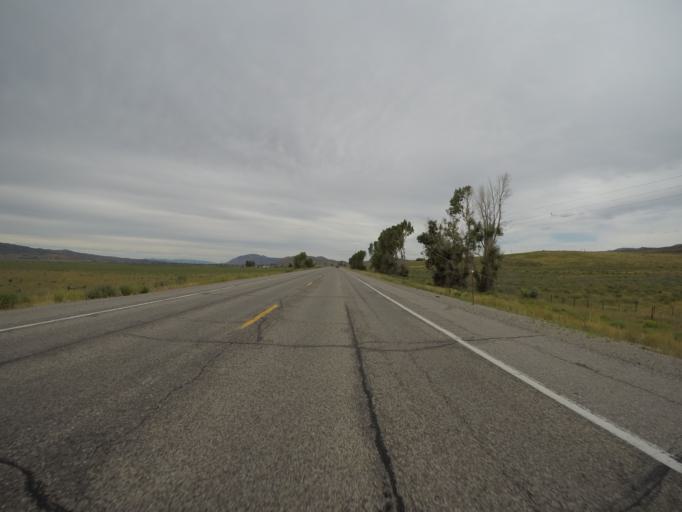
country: US
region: Utah
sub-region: Rich County
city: Randolph
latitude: 42.0417
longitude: -110.9315
